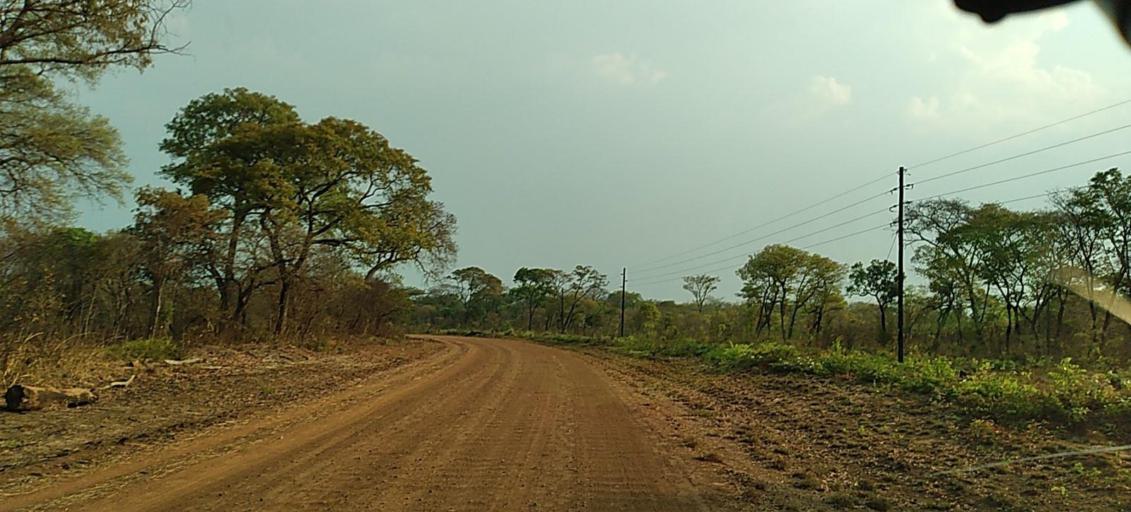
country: ZM
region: Western
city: Lukulu
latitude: -13.9940
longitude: 23.6155
